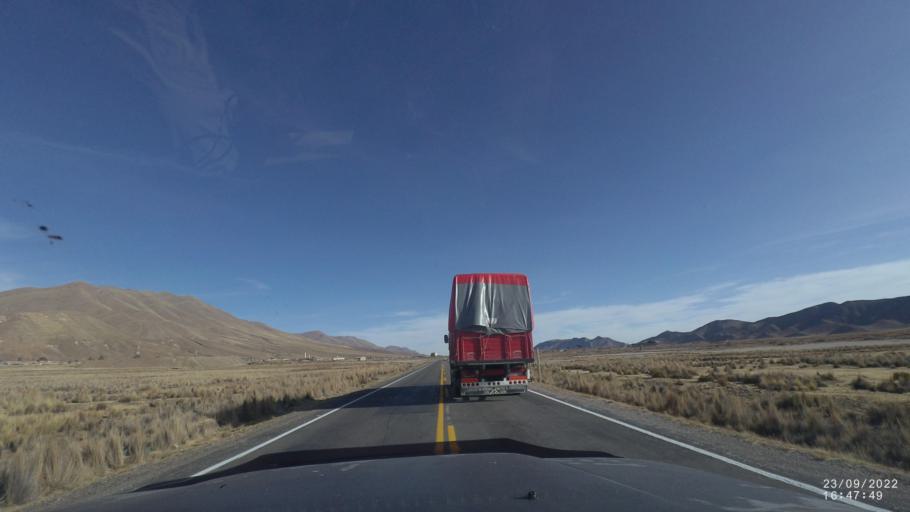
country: BO
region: Oruro
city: Poopo
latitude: -18.3728
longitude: -66.9803
